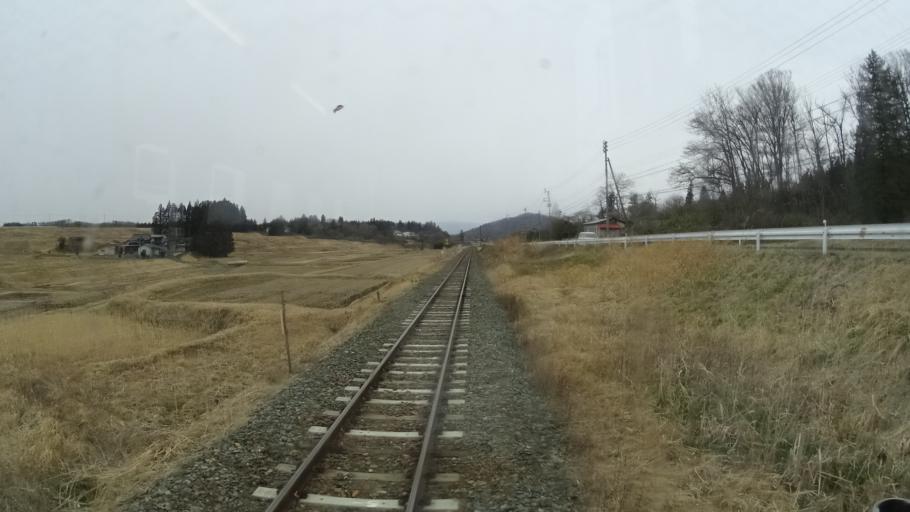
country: JP
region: Iwate
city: Hanamaki
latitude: 39.3990
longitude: 141.2086
